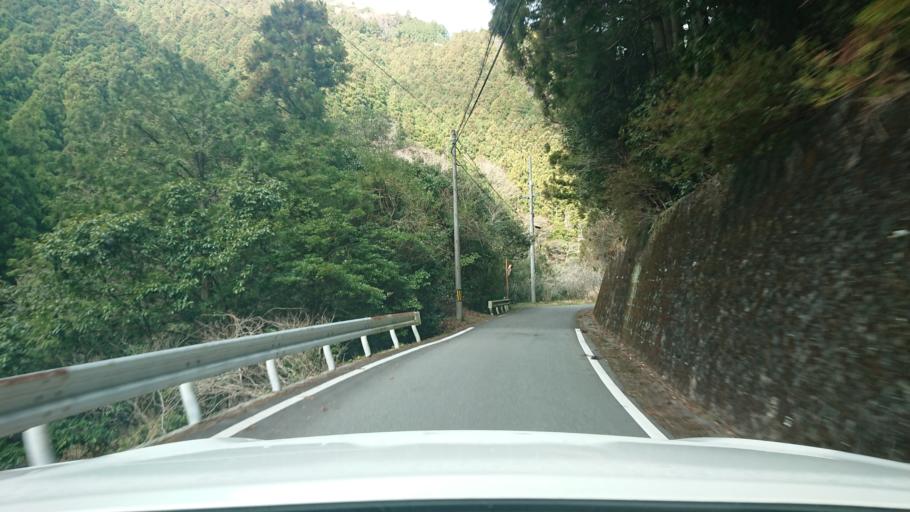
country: JP
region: Tokushima
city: Kamojimacho-jogejima
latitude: 33.9067
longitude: 134.3953
